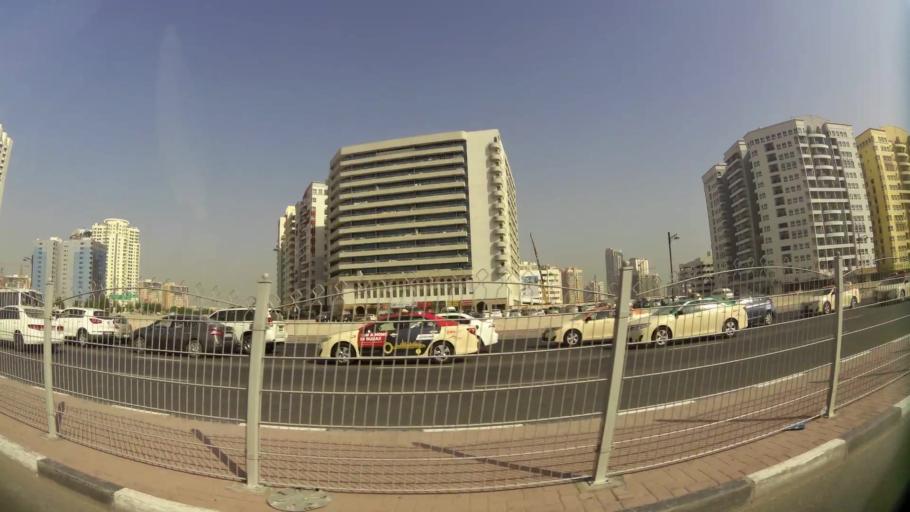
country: AE
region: Ash Shariqah
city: Sharjah
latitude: 25.2892
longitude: 55.3675
